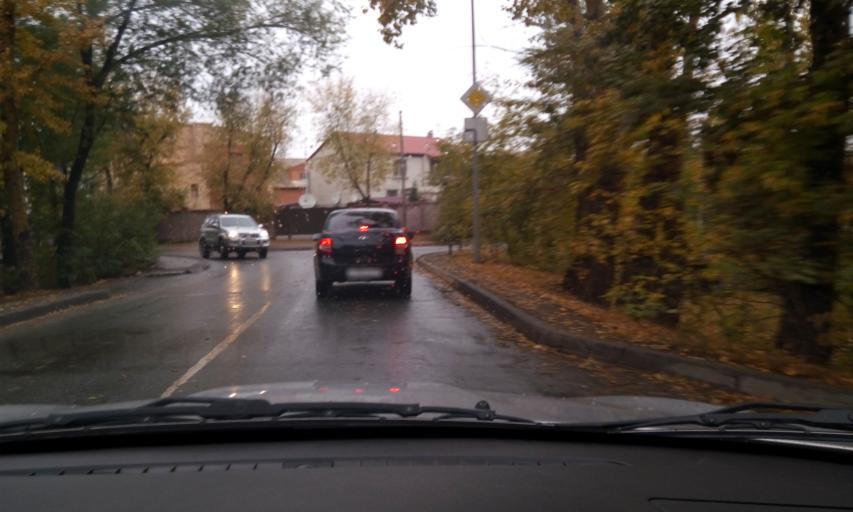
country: KZ
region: Astana Qalasy
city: Astana
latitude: 51.1441
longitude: 71.4309
